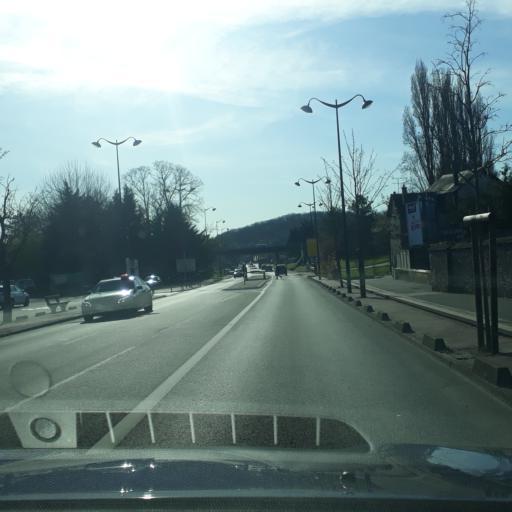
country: FR
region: Ile-de-France
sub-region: Departement de l'Essonne
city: Etampes
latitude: 48.4358
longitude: 2.1662
